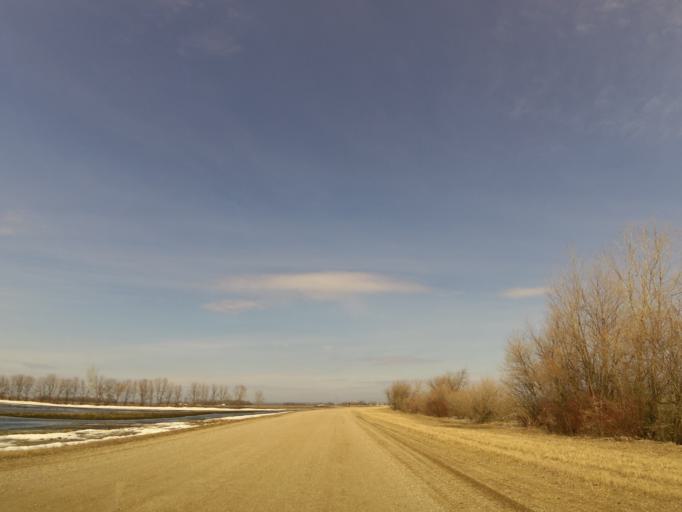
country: US
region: North Dakota
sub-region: Walsh County
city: Grafton
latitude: 48.4363
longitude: -97.4055
